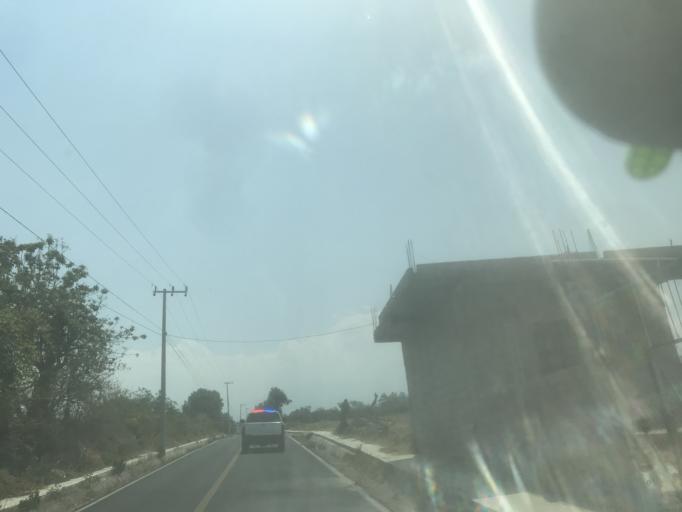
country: MX
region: Mexico
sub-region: Atlautla
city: San Andres Tlalamac
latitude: 18.9638
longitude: -98.8228
